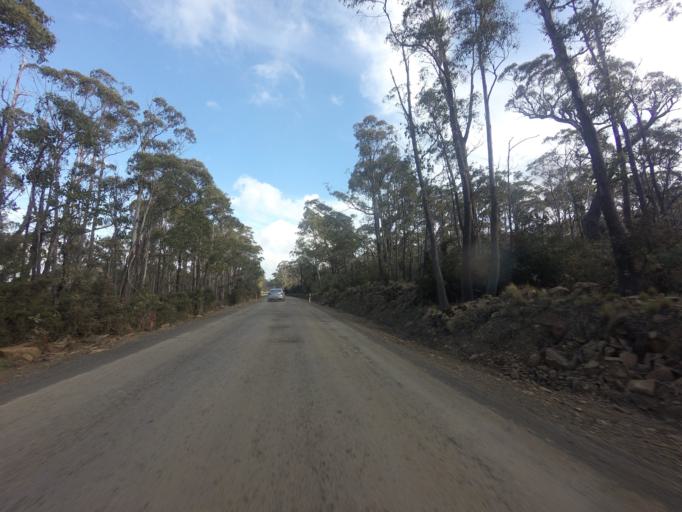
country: AU
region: Tasmania
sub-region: Meander Valley
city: Deloraine
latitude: -41.7808
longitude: 146.7069
